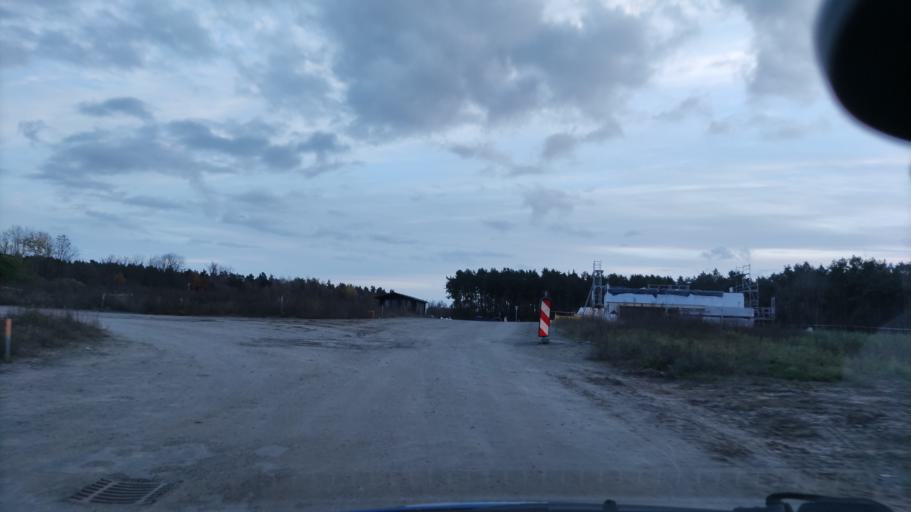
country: DE
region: Lower Saxony
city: Bad Bevensen
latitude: 53.0716
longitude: 10.6000
